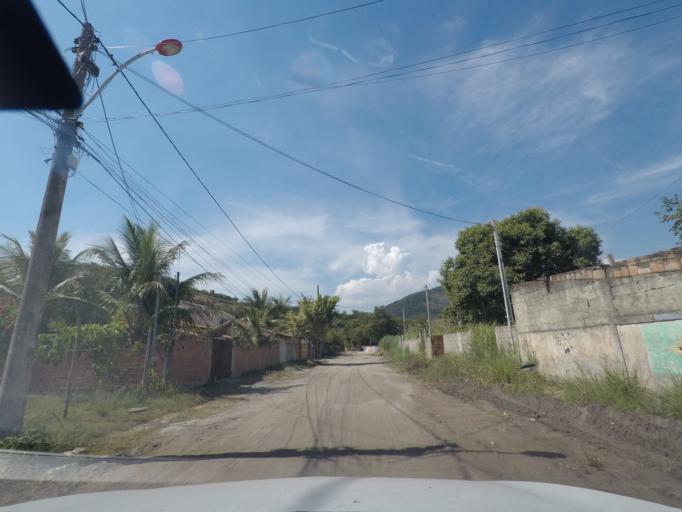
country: BR
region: Rio de Janeiro
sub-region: Niteroi
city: Niteroi
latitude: -22.9576
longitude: -42.9685
